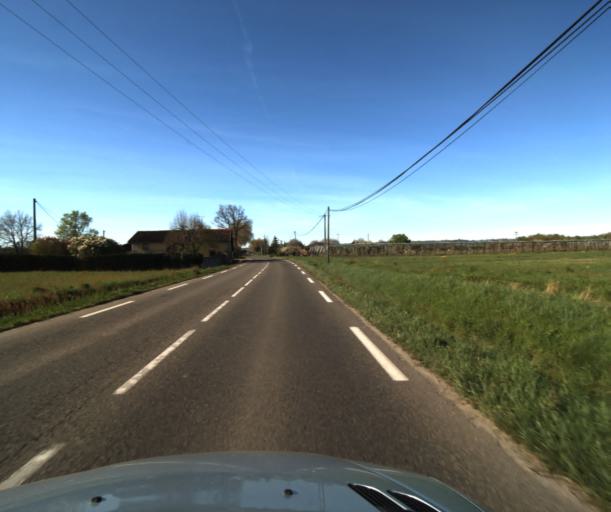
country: FR
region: Midi-Pyrenees
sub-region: Departement du Tarn-et-Garonne
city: Montbeton
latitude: 44.0619
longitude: 1.2886
